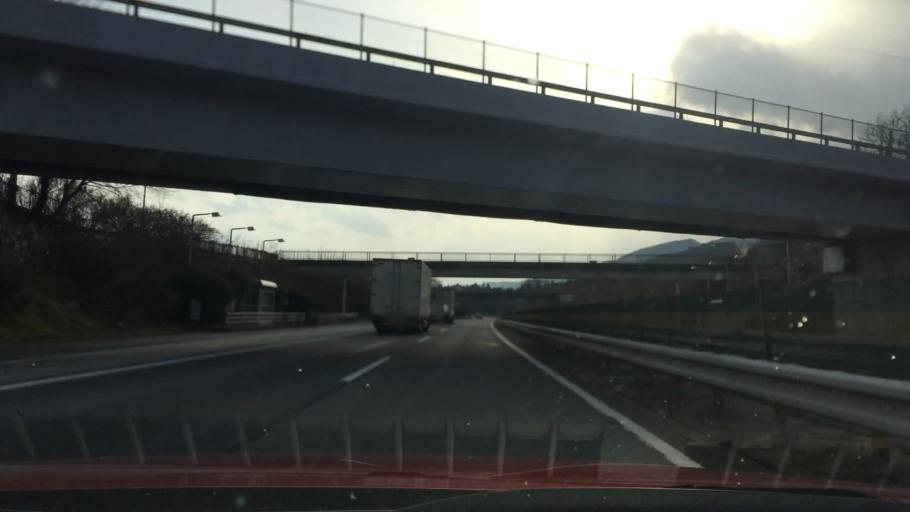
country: JP
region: Nagano
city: Ina
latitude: 35.6769
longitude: 137.9074
